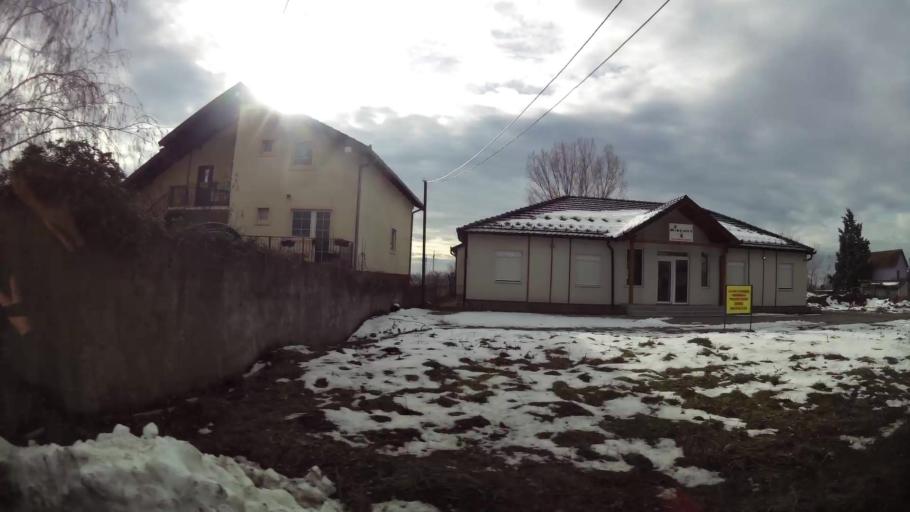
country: RS
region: Central Serbia
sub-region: Belgrade
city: Surcin
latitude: 44.7947
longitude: 20.3292
